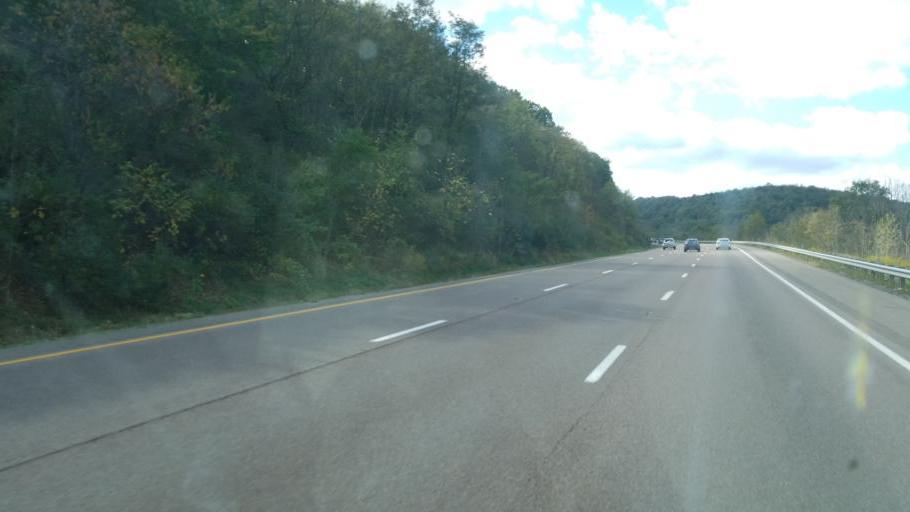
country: US
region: Maryland
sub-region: Allegany County
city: Frostburg
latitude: 39.6418
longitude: -78.8799
